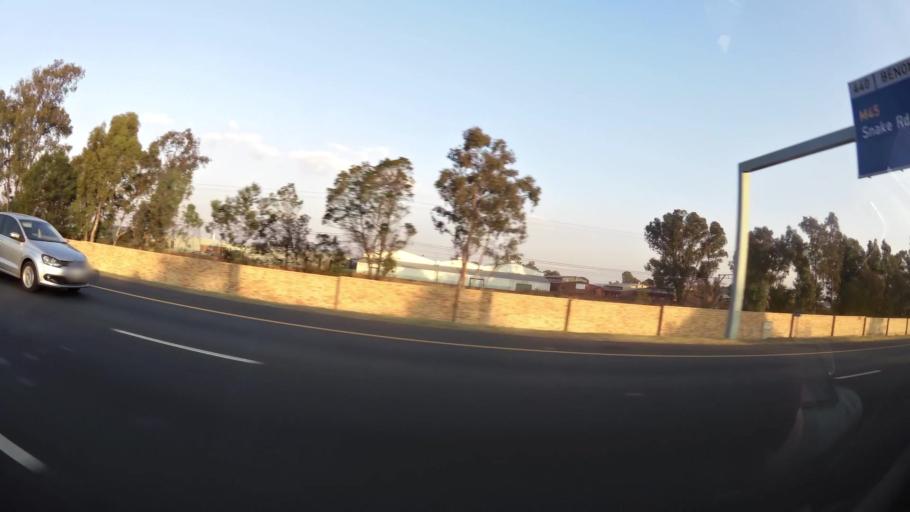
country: ZA
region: Gauteng
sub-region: Ekurhuleni Metropolitan Municipality
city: Benoni
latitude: -26.1720
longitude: 28.3456
